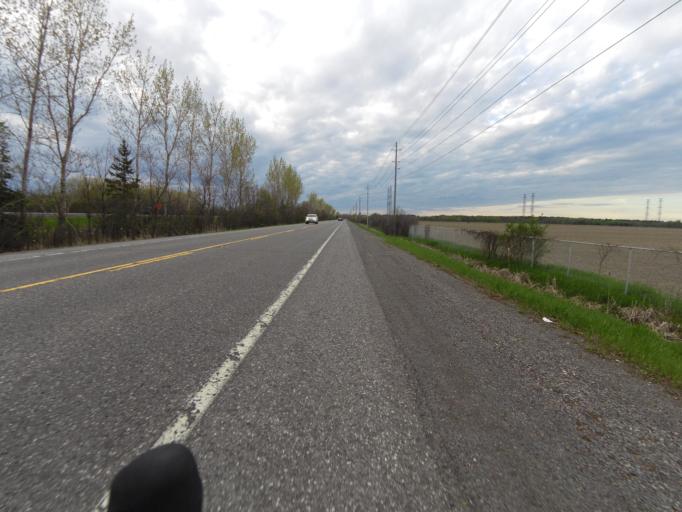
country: CA
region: Ontario
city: Bells Corners
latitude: 45.3042
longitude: -75.7935
